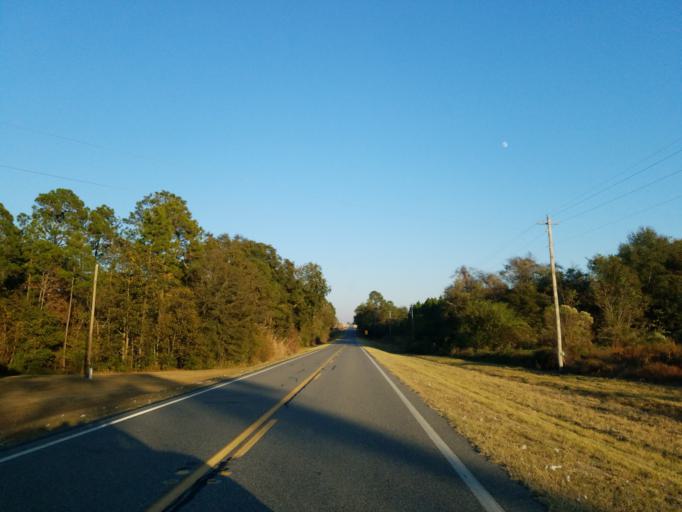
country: US
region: Georgia
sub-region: Turner County
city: Ashburn
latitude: 31.8595
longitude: -83.6166
